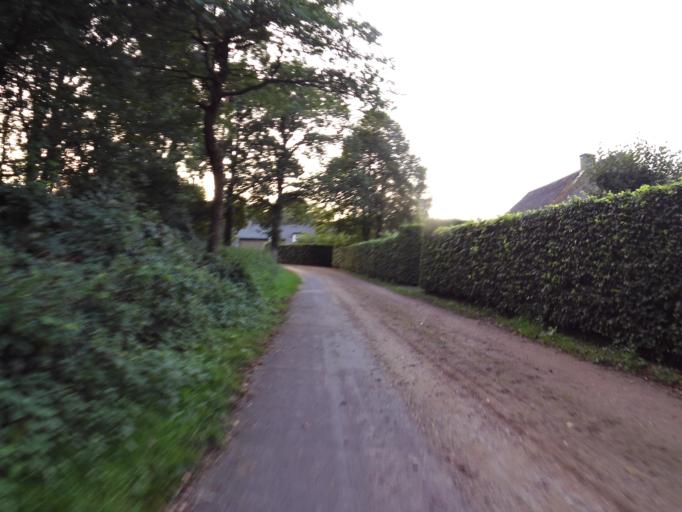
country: NL
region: Gelderland
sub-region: Gemeente Nijmegen
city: Lindenholt
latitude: 51.7980
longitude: 5.7765
